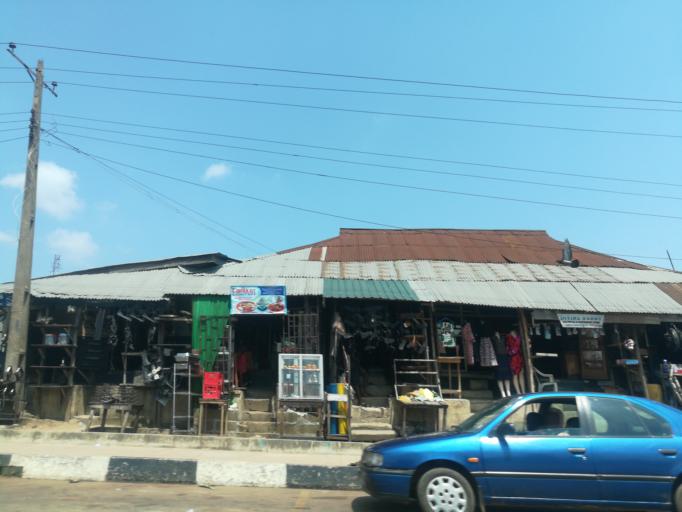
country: NG
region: Ogun
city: Abeokuta
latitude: 7.1502
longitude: 3.3551
